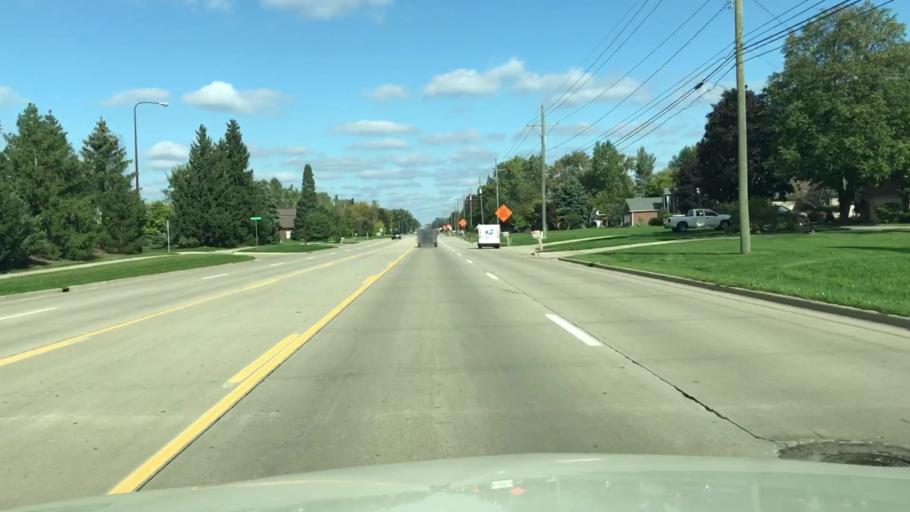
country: US
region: Michigan
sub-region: Macomb County
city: Sterling Heights
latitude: 42.5833
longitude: -83.0895
